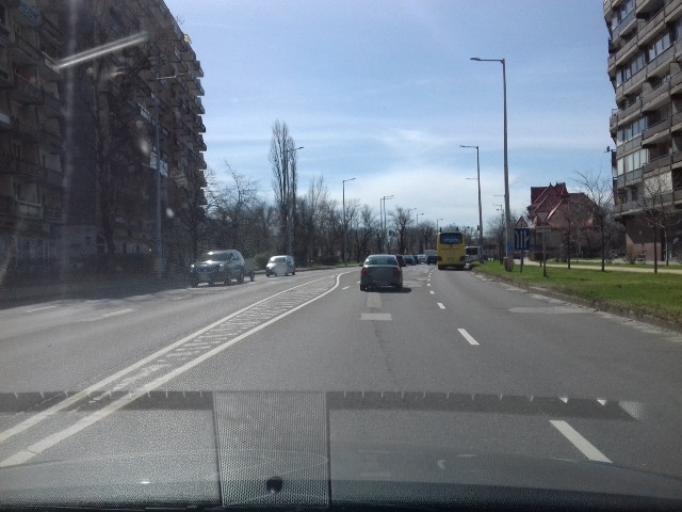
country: HU
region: Bacs-Kiskun
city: Kecskemet
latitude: 46.9036
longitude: 19.6853
